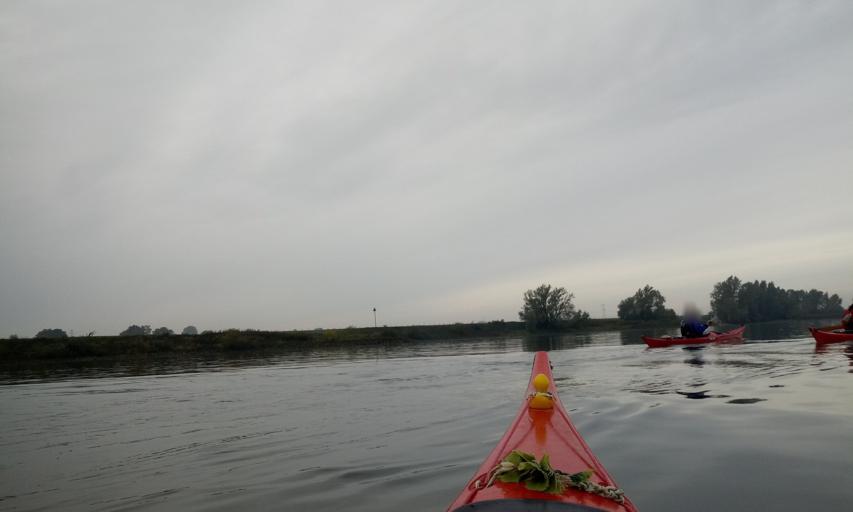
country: NL
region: Gelderland
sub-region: Gemeente Duiven
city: Duiven
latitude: 51.9070
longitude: 5.9985
